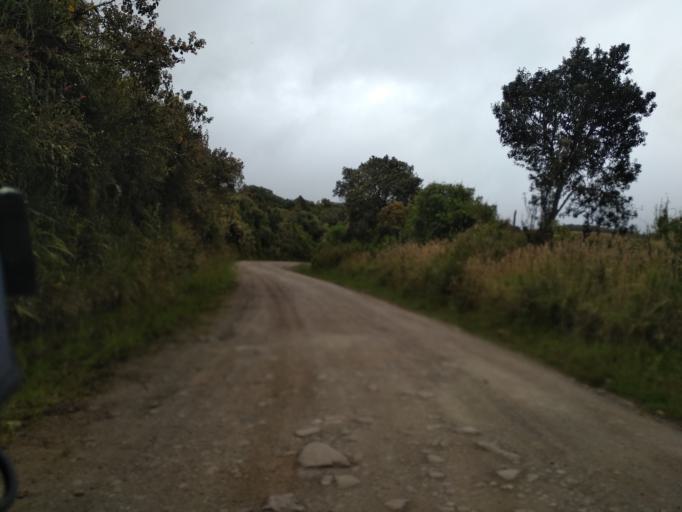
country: EC
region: Carchi
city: Tulcan
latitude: 0.7444
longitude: -77.7820
